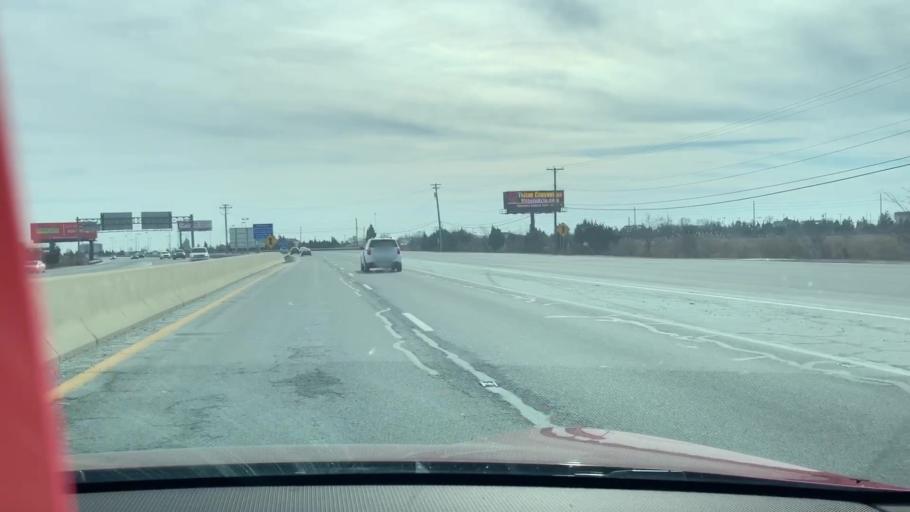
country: US
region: New Jersey
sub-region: Atlantic County
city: Pleasantville
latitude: 39.3908
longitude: -74.5099
